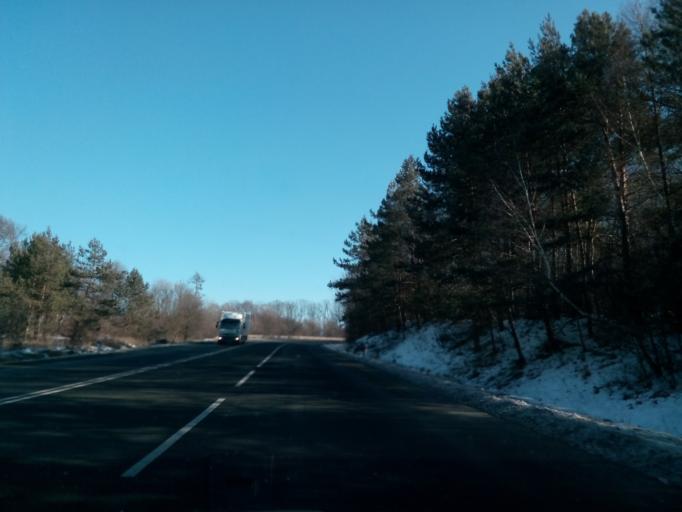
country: SK
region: Kosicky
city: Secovce
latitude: 48.7425
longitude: 21.5260
